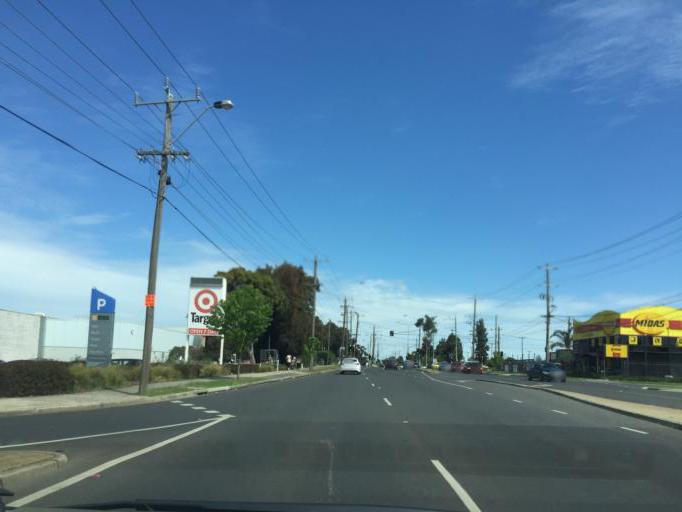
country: AU
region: Victoria
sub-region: Maribyrnong
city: Maribyrnong
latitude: -37.7744
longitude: 144.8858
